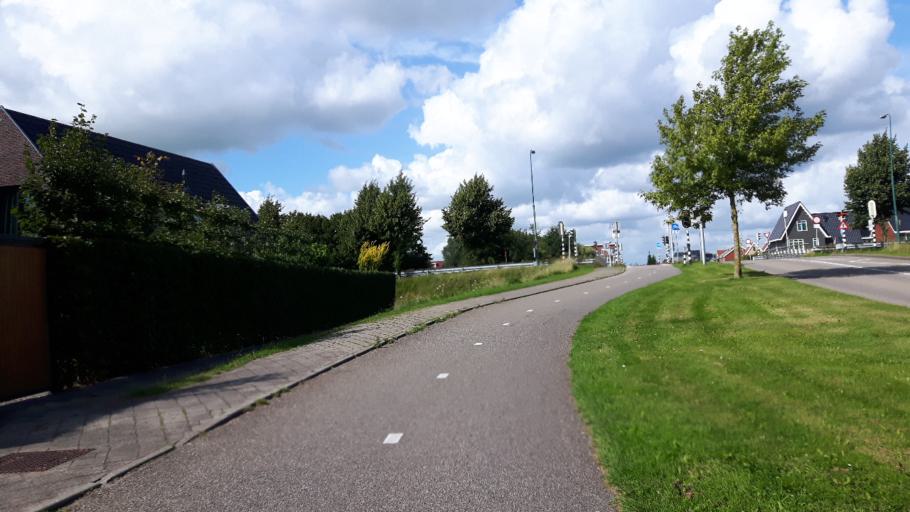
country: NL
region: Utrecht
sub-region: Stichtse Vecht
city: Spechtenkamp
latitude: 52.0866
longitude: 5.0117
